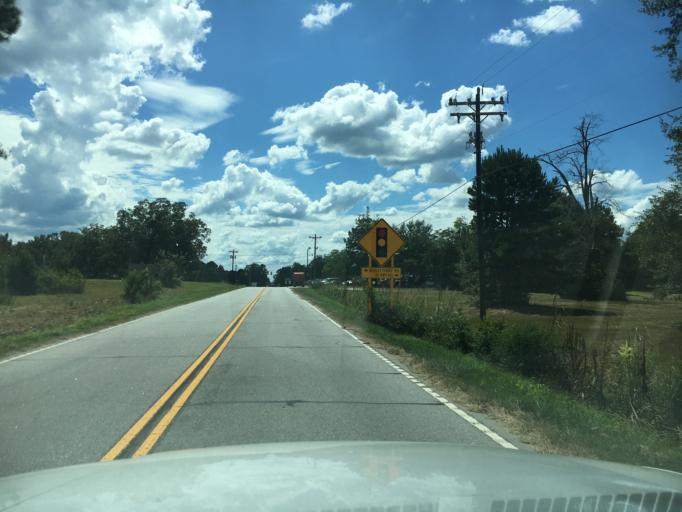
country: US
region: South Carolina
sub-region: Greenwood County
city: Ware Shoals
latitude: 34.5226
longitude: -82.1870
